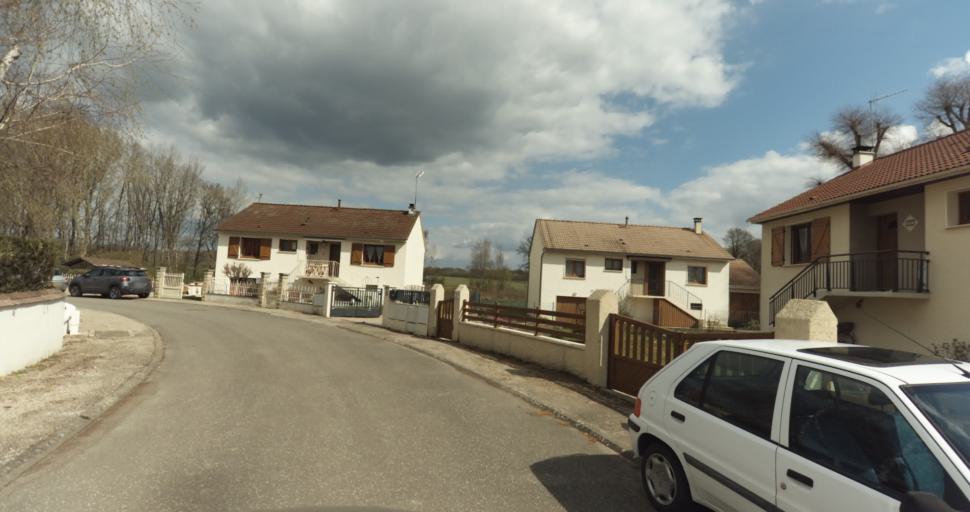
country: FR
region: Bourgogne
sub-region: Departement de la Cote-d'Or
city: Auxonne
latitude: 47.1880
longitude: 5.4138
